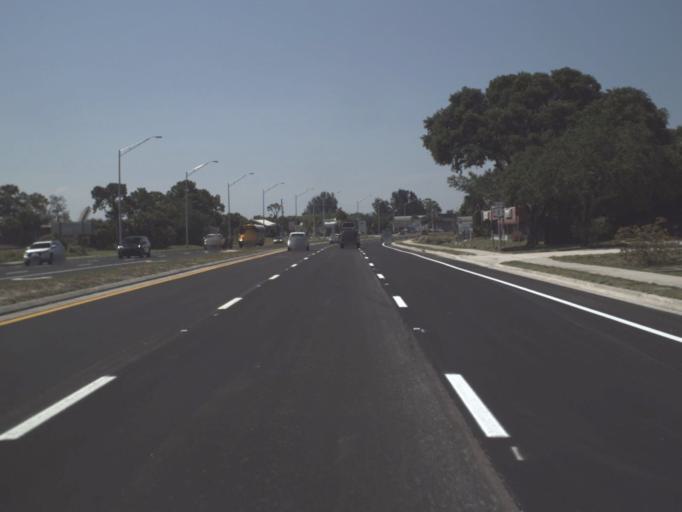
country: US
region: Florida
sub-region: Brevard County
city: Indian Harbour Beach
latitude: 28.1485
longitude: -80.6384
